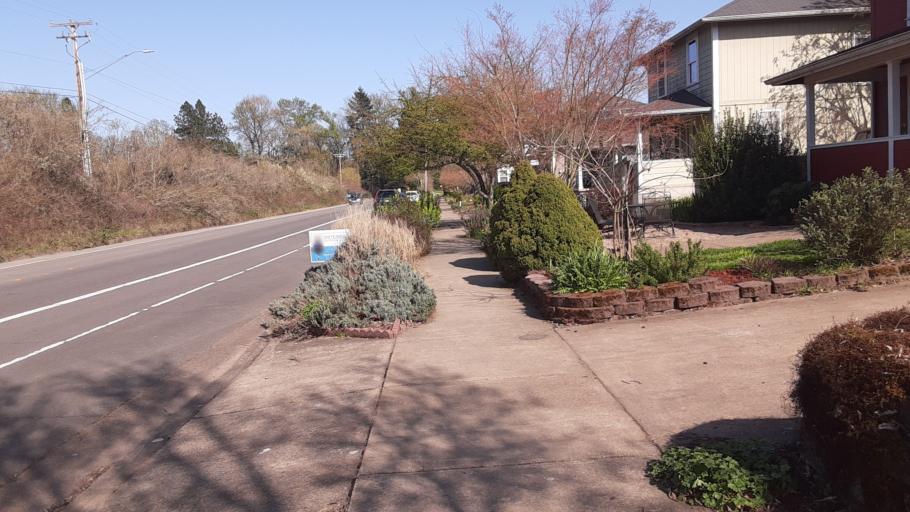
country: US
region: Oregon
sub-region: Benton County
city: Corvallis
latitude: 44.5367
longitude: -123.2556
